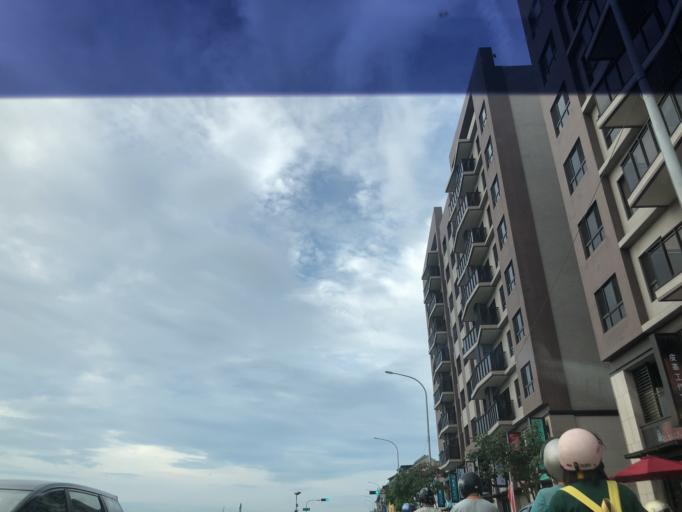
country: TW
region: Taiwan
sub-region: Taichung City
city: Taichung
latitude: 24.1012
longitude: 120.6947
